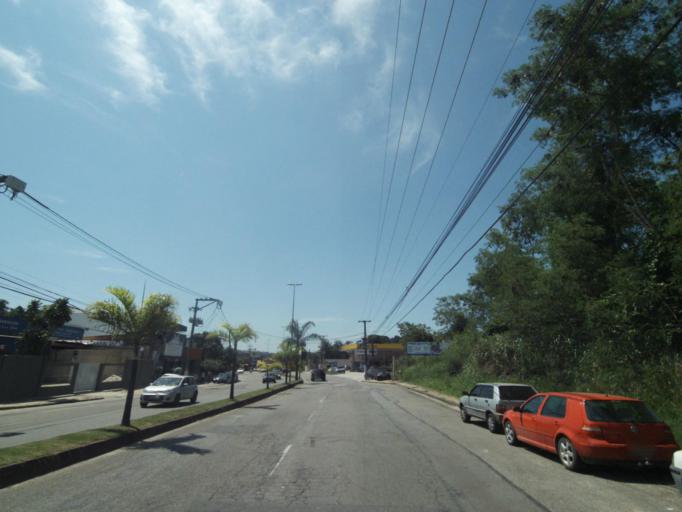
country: BR
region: Rio de Janeiro
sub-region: Sao Goncalo
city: Sao Goncalo
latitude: -22.8887
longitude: -43.0336
